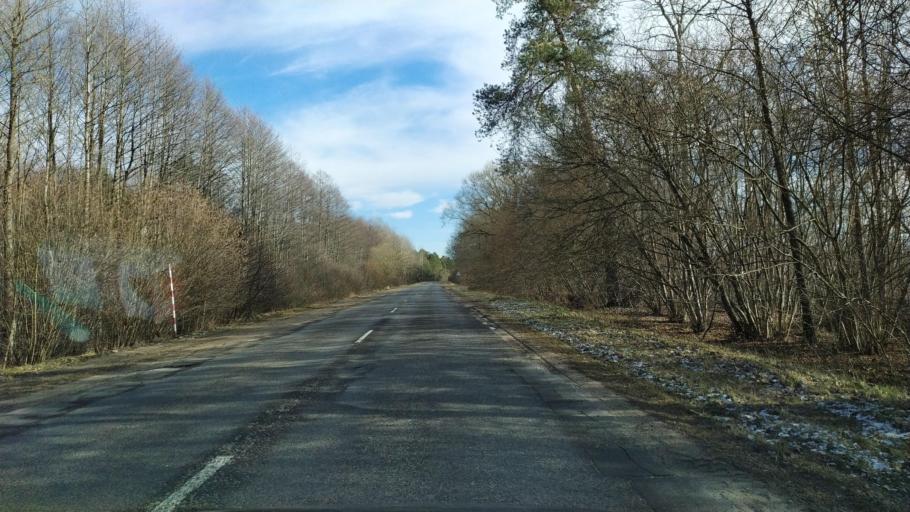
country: BY
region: Brest
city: Pruzhany
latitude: 52.5768
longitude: 24.2948
